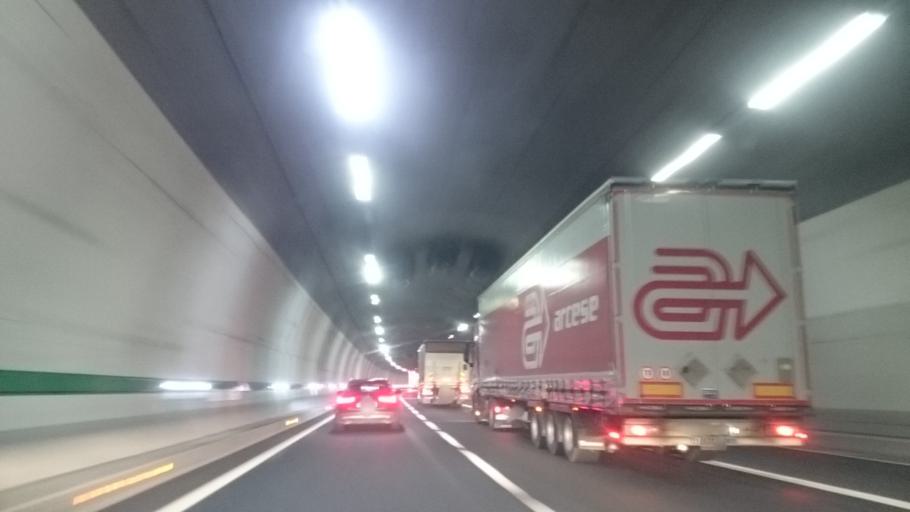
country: IT
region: Emilia-Romagna
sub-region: Provincia di Bologna
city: Castiglione dei Pepoli
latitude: 44.1669
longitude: 11.1966
